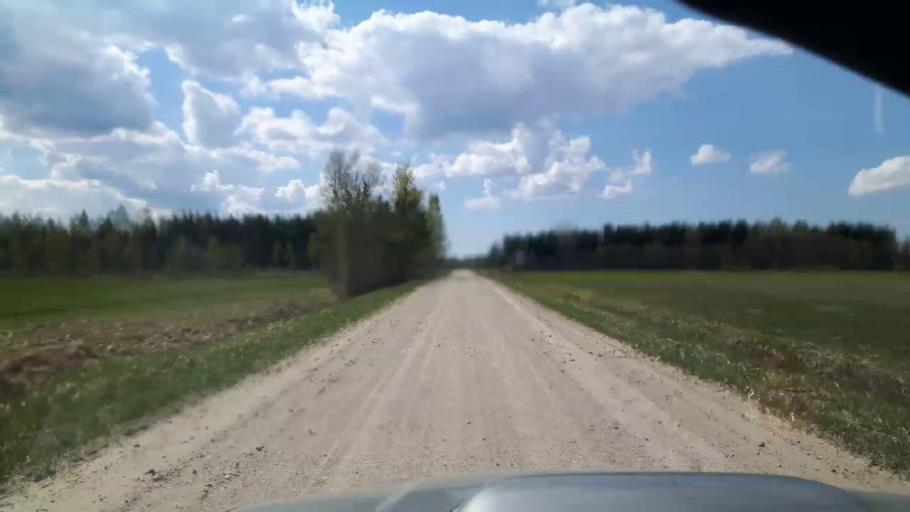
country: EE
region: Paernumaa
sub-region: Tootsi vald
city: Tootsi
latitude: 58.4590
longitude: 24.8809
